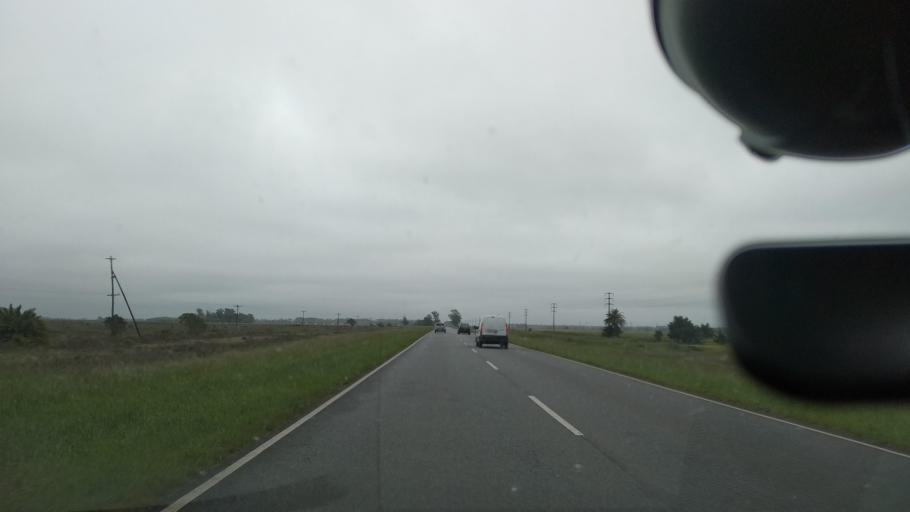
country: AR
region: Buenos Aires
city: Veronica
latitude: -35.3435
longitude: -57.4465
